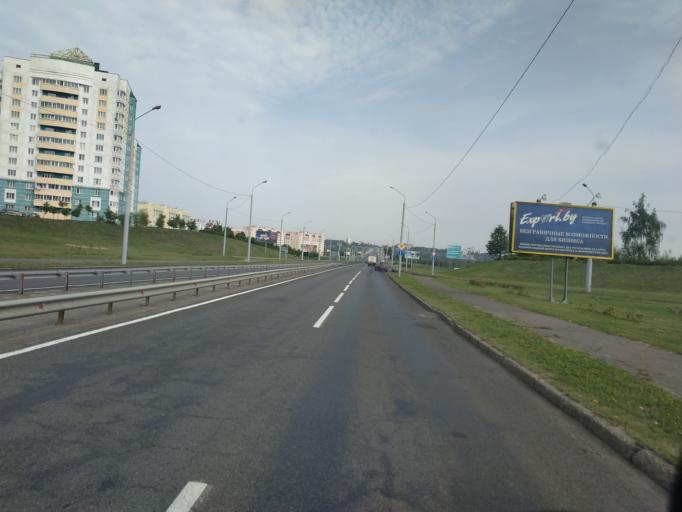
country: BY
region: Mogilev
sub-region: Mahilyowski Rayon
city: Veyno
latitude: 53.8790
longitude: 30.3836
